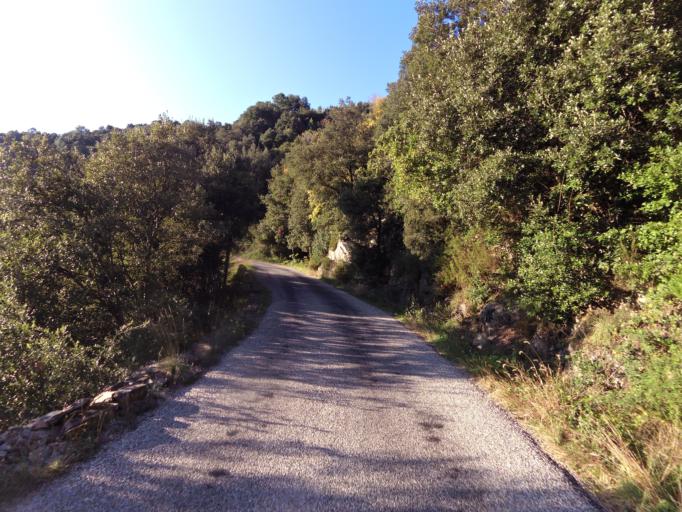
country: FR
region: Rhone-Alpes
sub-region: Departement de l'Ardeche
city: Lablachere
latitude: 44.5218
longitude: 4.1793
